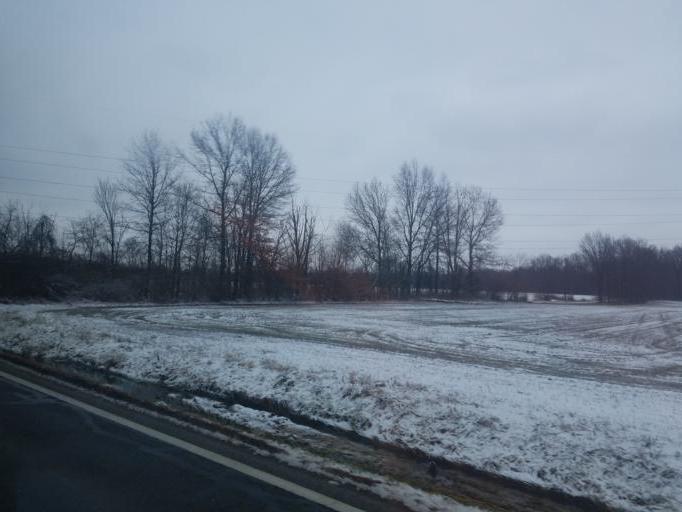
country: US
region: Ohio
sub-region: Franklin County
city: New Albany
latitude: 40.0374
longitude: -82.7881
